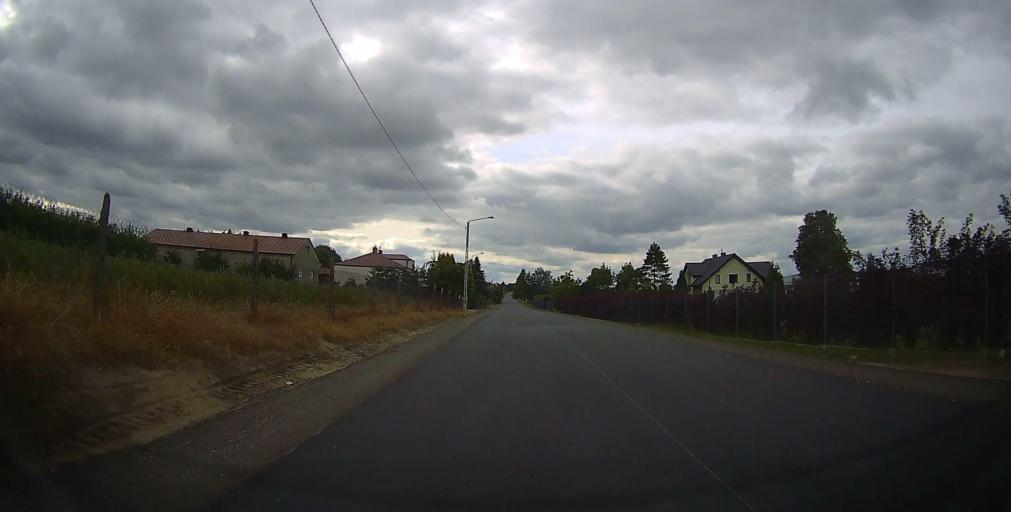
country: PL
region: Masovian Voivodeship
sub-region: Powiat grojecki
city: Belsk Duzy
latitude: 51.8066
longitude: 20.8562
